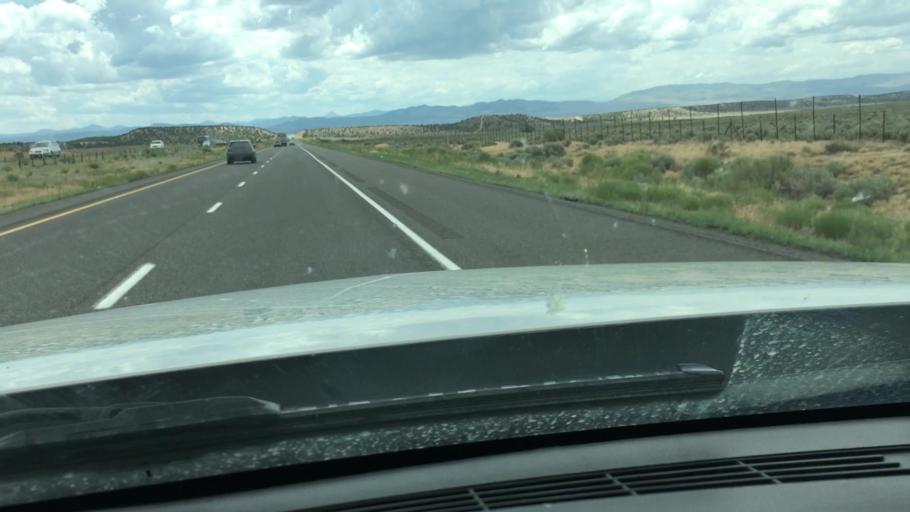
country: US
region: Utah
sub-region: Beaver County
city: Beaver
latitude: 38.3535
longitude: -112.6606
